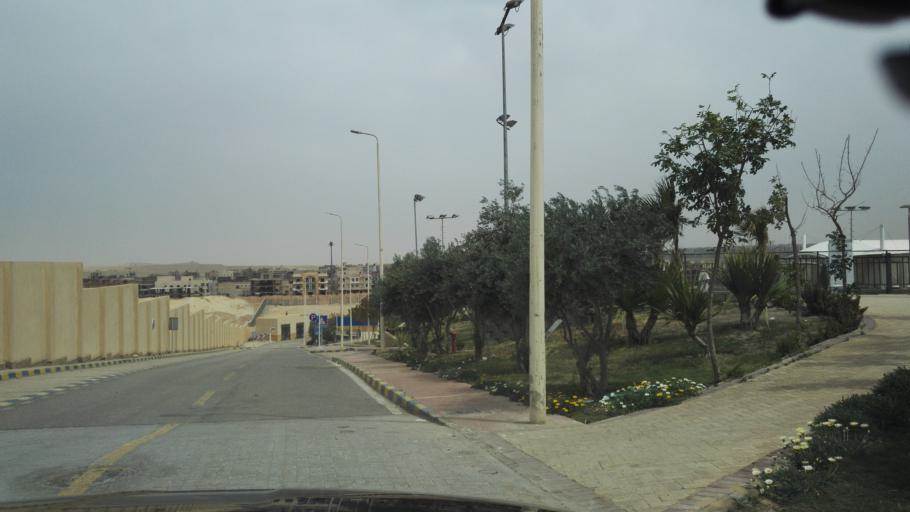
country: EG
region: Muhafazat al Qalyubiyah
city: Al Khankah
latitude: 30.0400
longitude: 31.5271
